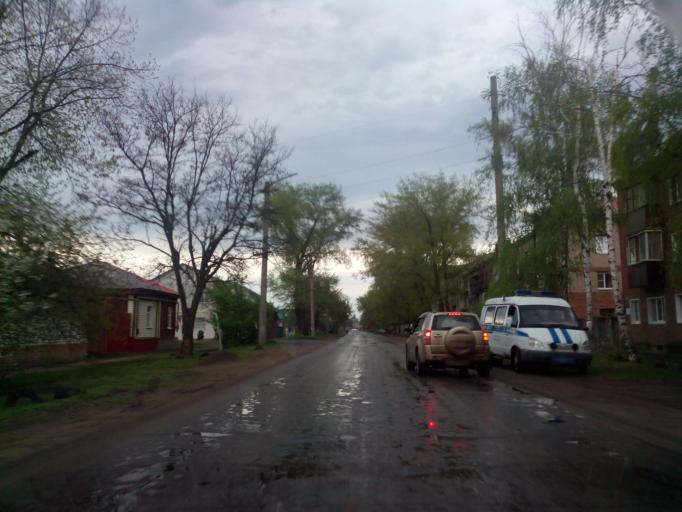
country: RU
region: Voronezj
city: Borisoglebsk
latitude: 51.3571
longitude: 42.0796
